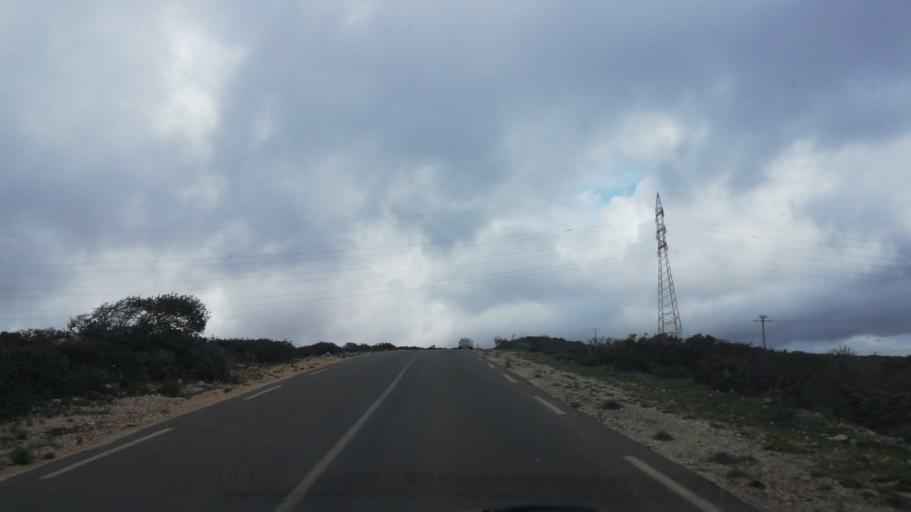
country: DZ
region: Oran
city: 'Ain el Turk
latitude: 35.6910
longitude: -0.7797
